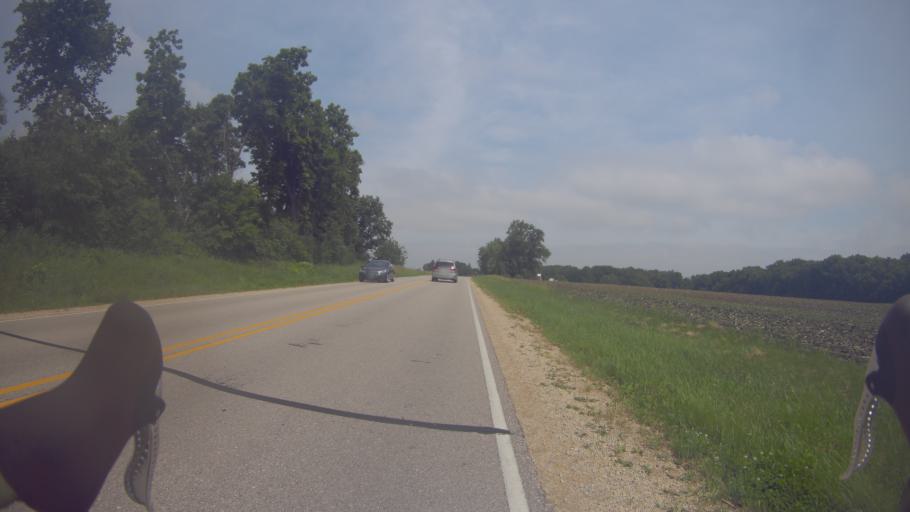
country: US
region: Wisconsin
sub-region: Rock County
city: Edgerton
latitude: 42.8725
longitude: -89.0363
